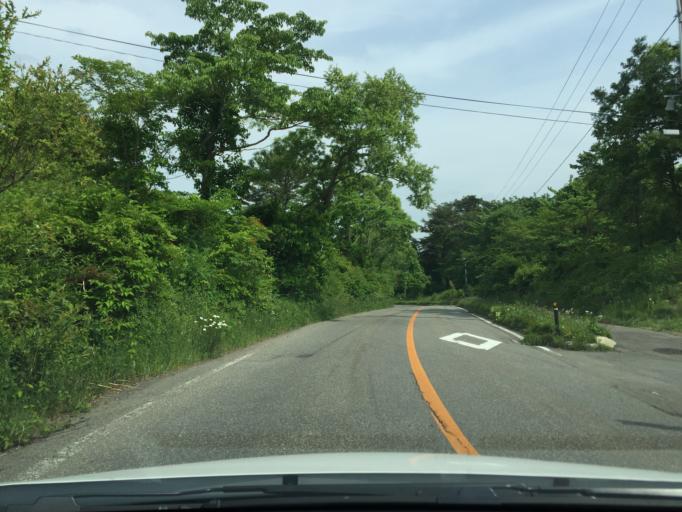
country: JP
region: Fukushima
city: Inawashiro
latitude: 37.6724
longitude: 140.0759
